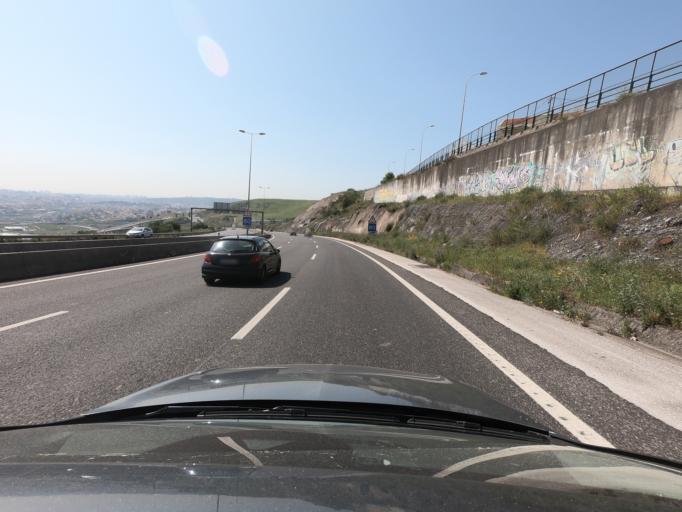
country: PT
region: Lisbon
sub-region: Odivelas
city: Famoes
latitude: 38.7804
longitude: -9.2292
